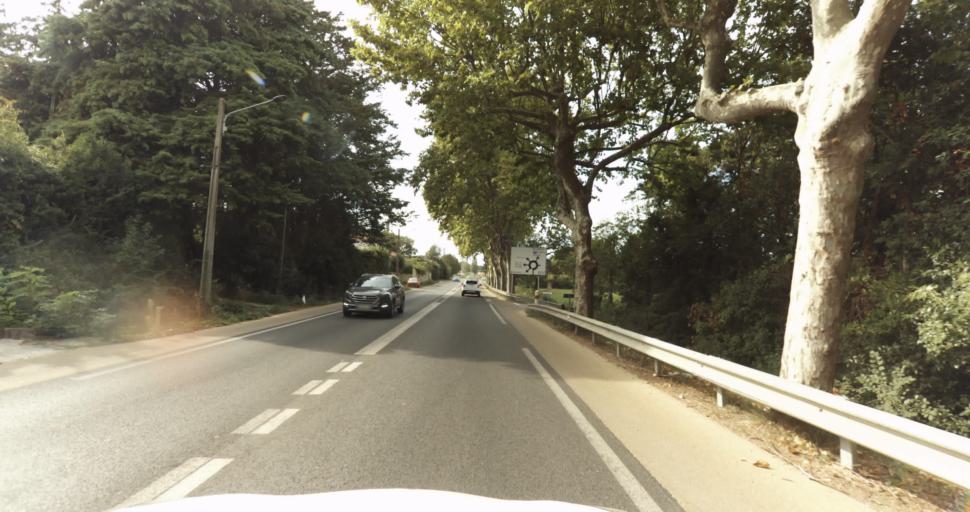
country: FR
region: Provence-Alpes-Cote d'Azur
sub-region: Departement des Bouches-du-Rhone
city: Saint-Chamas
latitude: 43.5700
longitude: 5.0215
